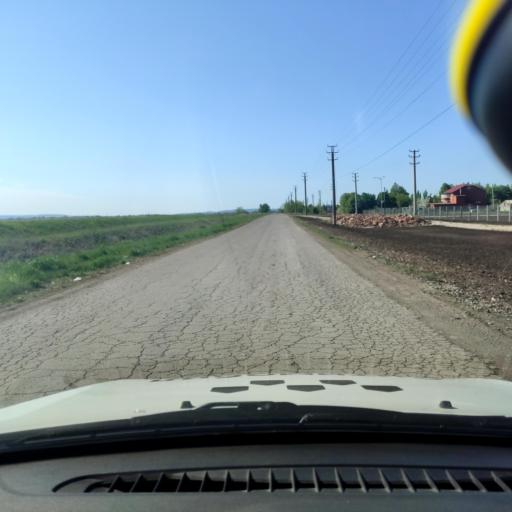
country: RU
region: Samara
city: Podstepki
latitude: 53.5390
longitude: 49.2001
